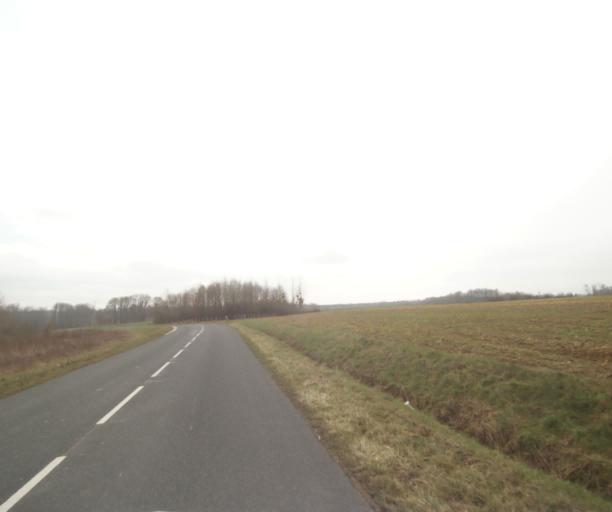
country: FR
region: Champagne-Ardenne
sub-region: Departement de la Marne
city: Pargny-sur-Saulx
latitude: 48.7437
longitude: 4.8599
